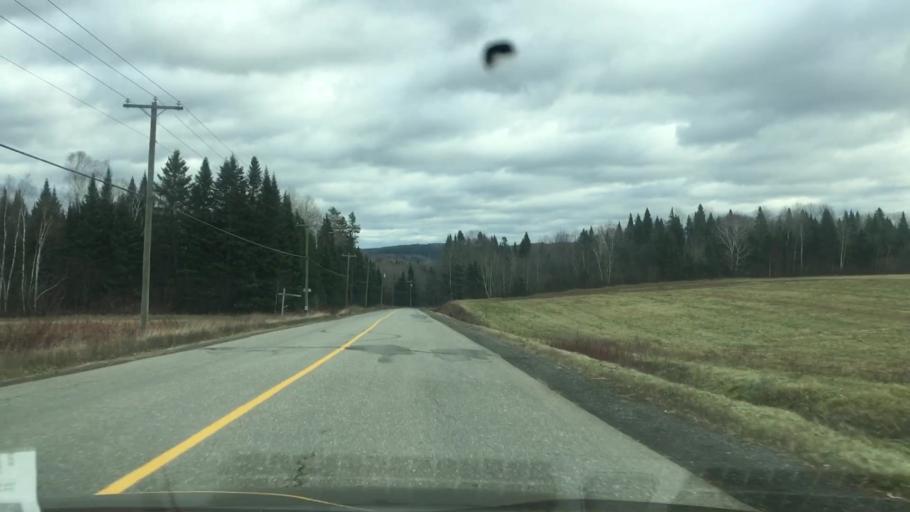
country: US
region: Maine
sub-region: Aroostook County
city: Fort Fairfield
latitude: 46.7504
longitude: -67.7326
